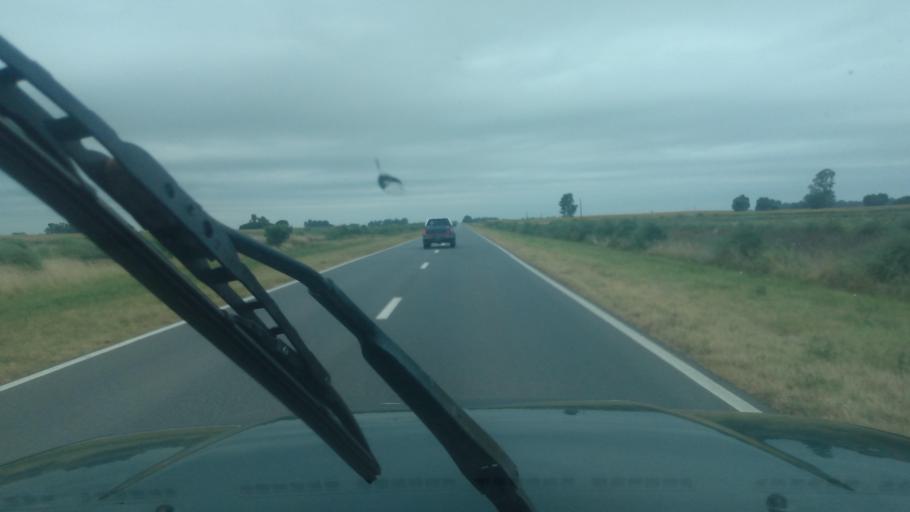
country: AR
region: Buenos Aires
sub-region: Partido de Bragado
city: Bragado
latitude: -35.3183
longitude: -60.6350
